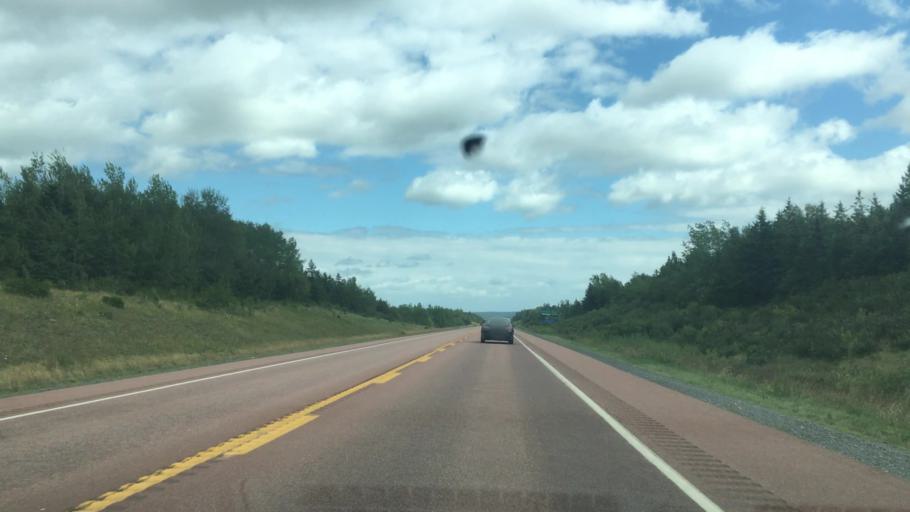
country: CA
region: Nova Scotia
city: Port Hawkesbury
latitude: 45.6074
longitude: -61.6661
